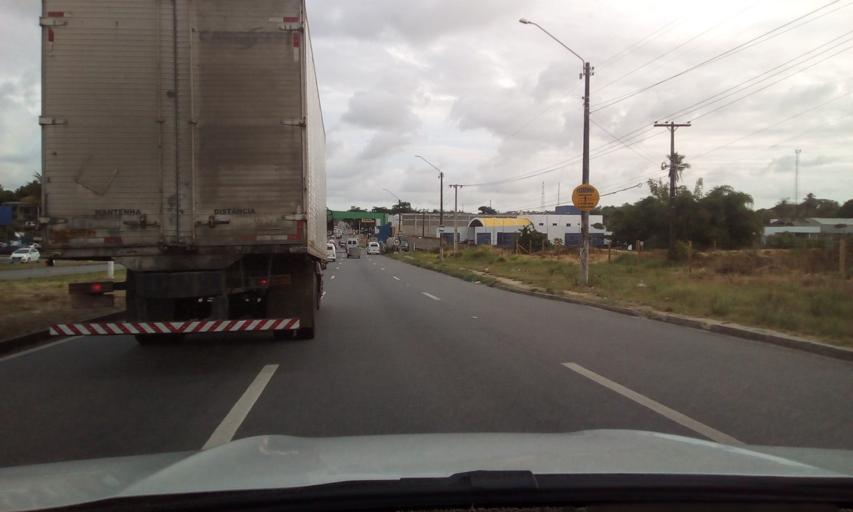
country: BR
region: Pernambuco
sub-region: Abreu E Lima
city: Abreu e Lima
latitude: -7.8850
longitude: -34.9046
